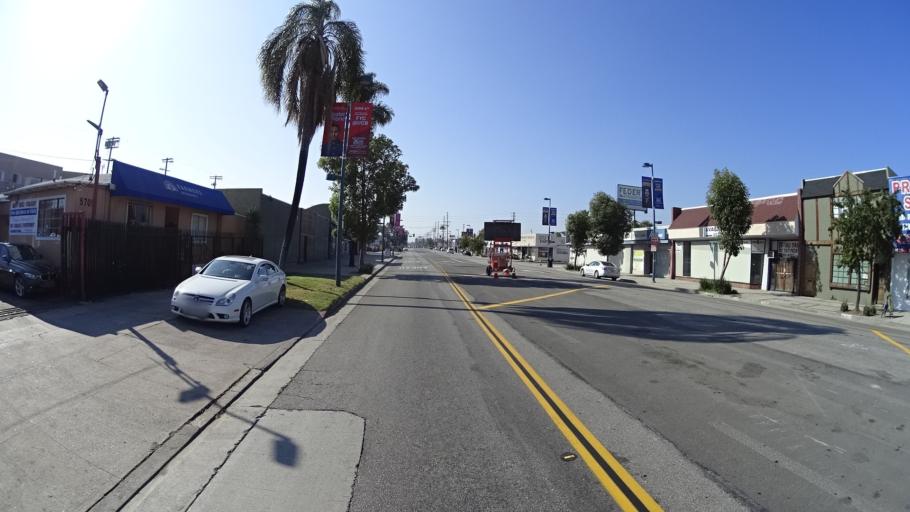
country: US
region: California
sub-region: Los Angeles County
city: North Hollywood
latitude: 34.1745
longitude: -118.3804
